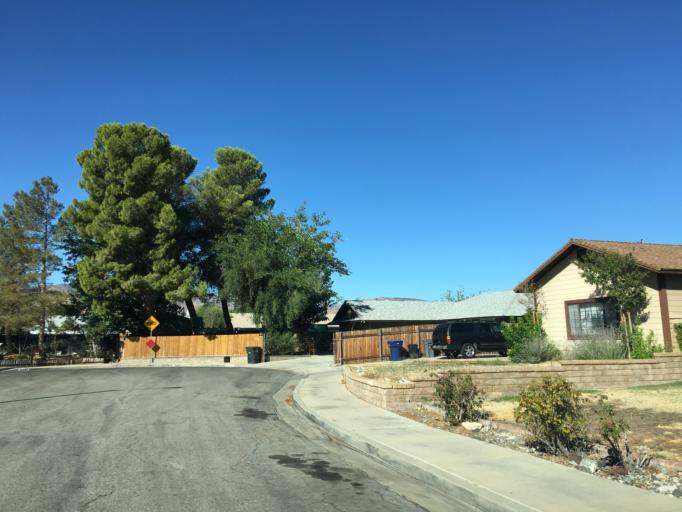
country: US
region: California
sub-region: Los Angeles County
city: Desert View Highlands
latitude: 34.5924
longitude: -118.1554
